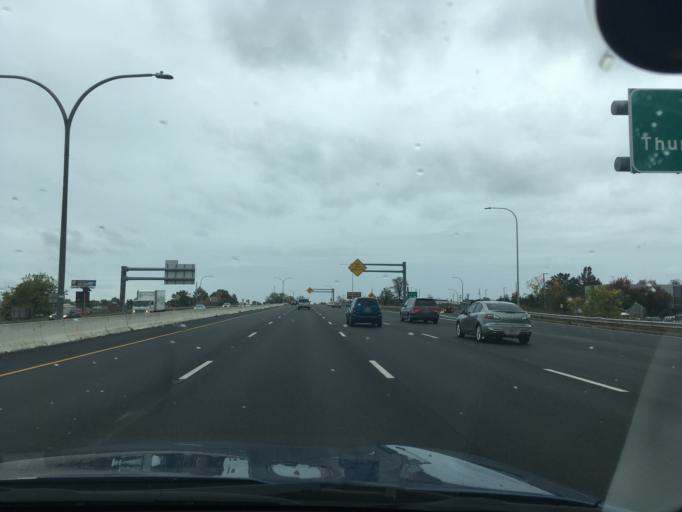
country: US
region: Rhode Island
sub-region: Providence County
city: Providence
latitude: 41.8028
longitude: -71.4039
